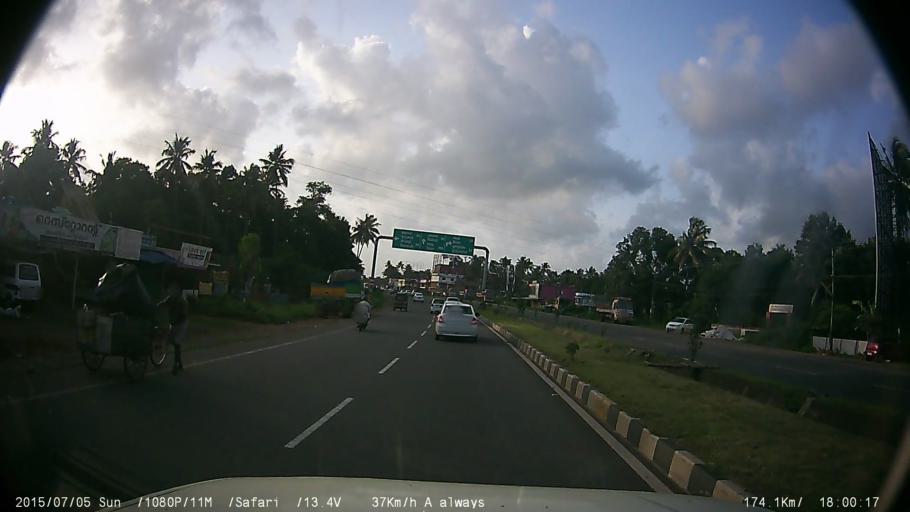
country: IN
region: Kerala
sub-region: Thrissur District
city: Kizhake Chalakudi
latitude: 10.2806
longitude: 76.3440
